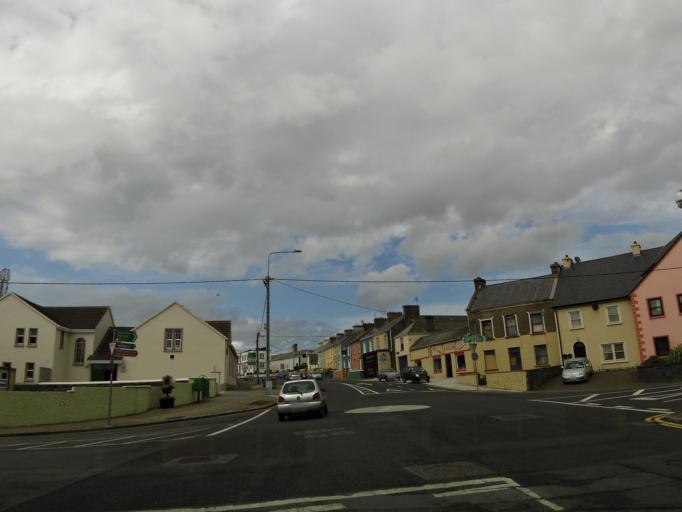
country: IE
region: Munster
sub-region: An Clar
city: Kilrush
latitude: 52.6401
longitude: -9.4854
